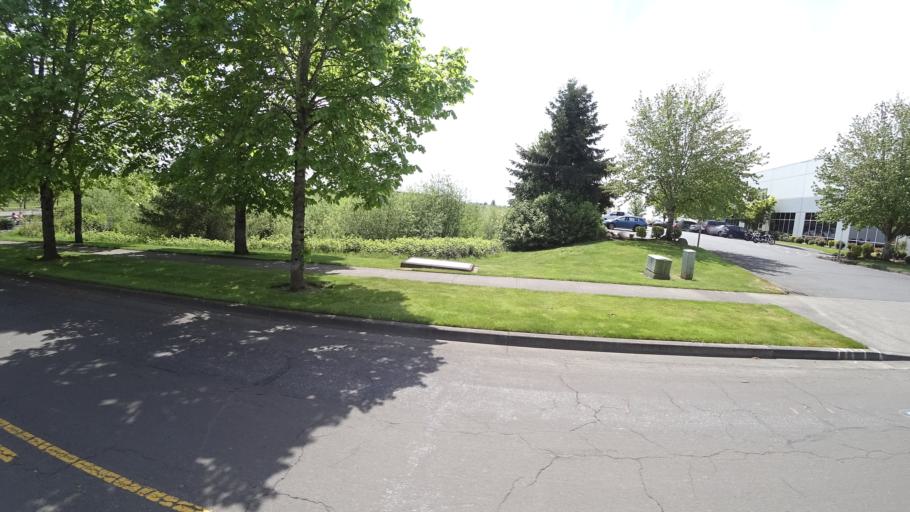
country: US
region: Oregon
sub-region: Washington County
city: Rockcreek
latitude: 45.5695
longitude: -122.9069
